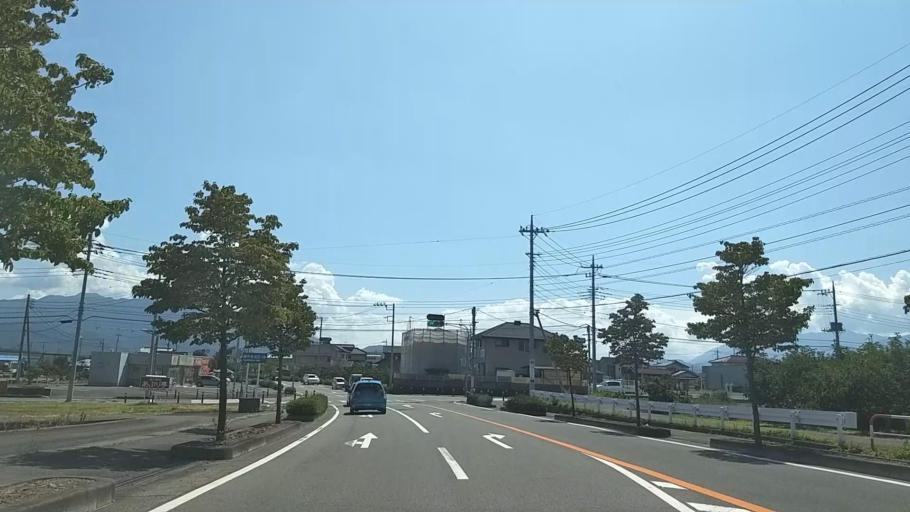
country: JP
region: Yamanashi
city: Ryuo
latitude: 35.6208
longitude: 138.4986
